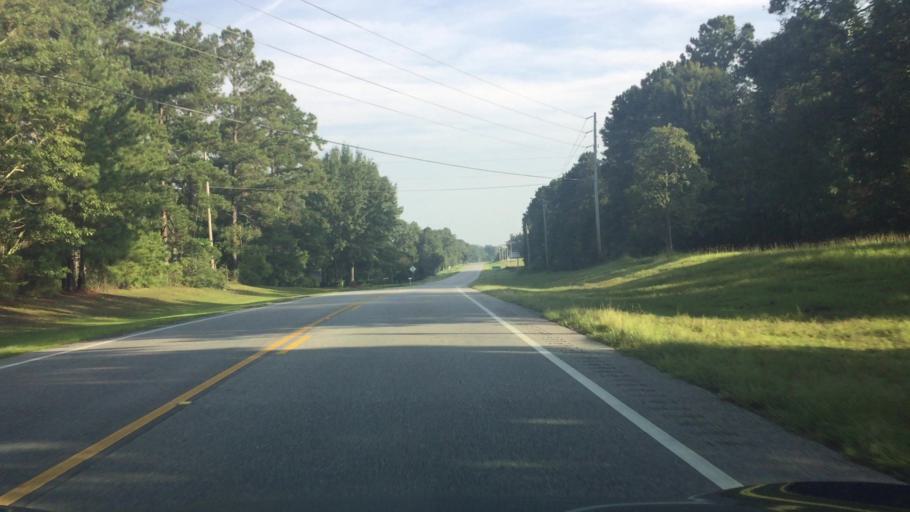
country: US
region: Alabama
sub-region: Covington County
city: Andalusia
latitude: 31.2604
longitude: -86.4706
